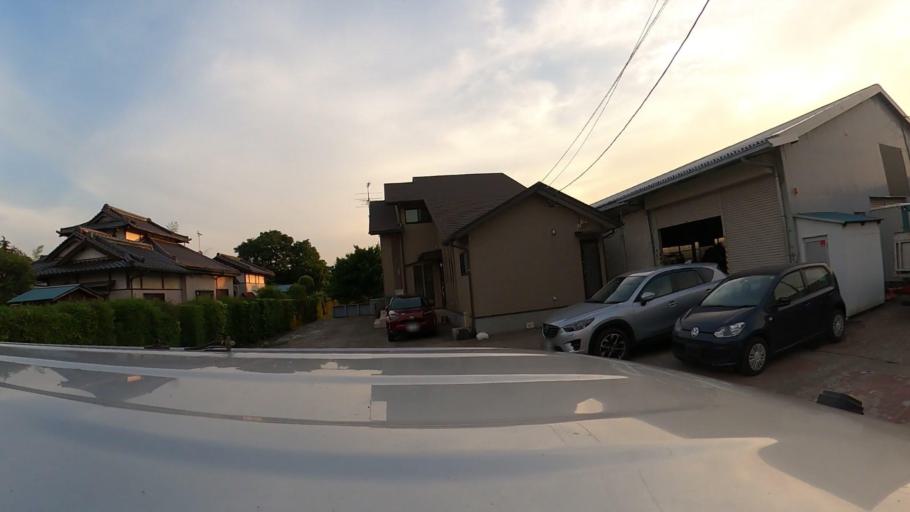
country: JP
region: Ibaraki
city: Ushiku
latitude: 36.0269
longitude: 140.0916
